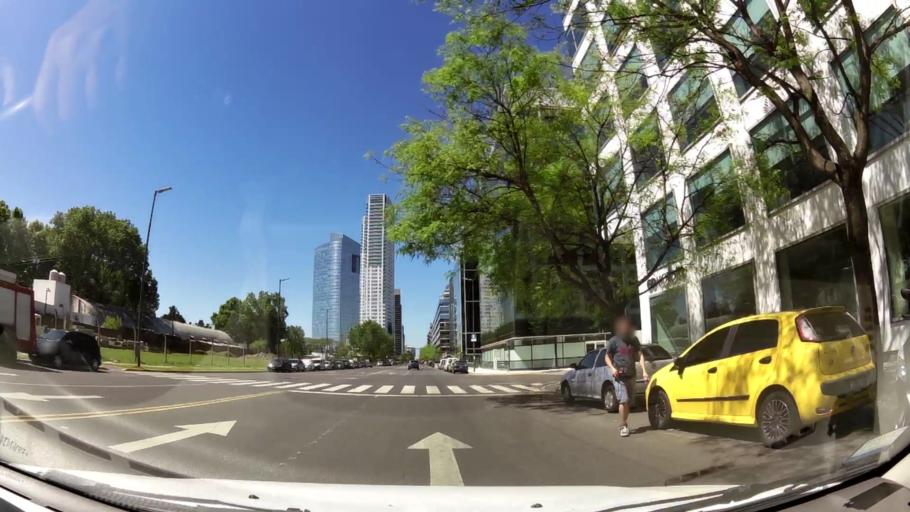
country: AR
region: Buenos Aires F.D.
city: Buenos Aires
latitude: -34.6007
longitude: -58.3638
